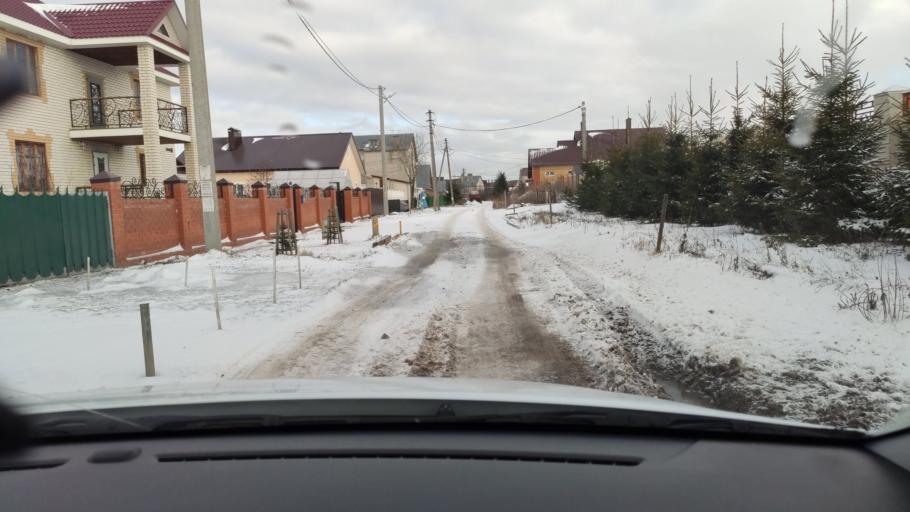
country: RU
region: Tatarstan
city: Stolbishchi
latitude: 55.7697
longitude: 49.2704
